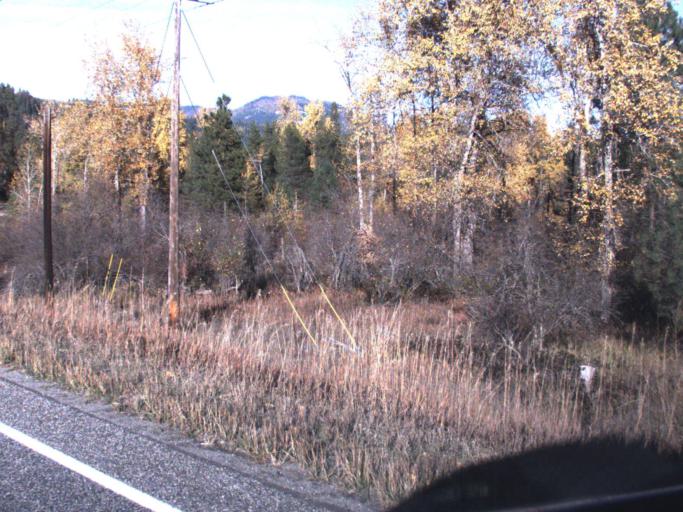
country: CA
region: British Columbia
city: Rossland
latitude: 48.9403
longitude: -117.7722
